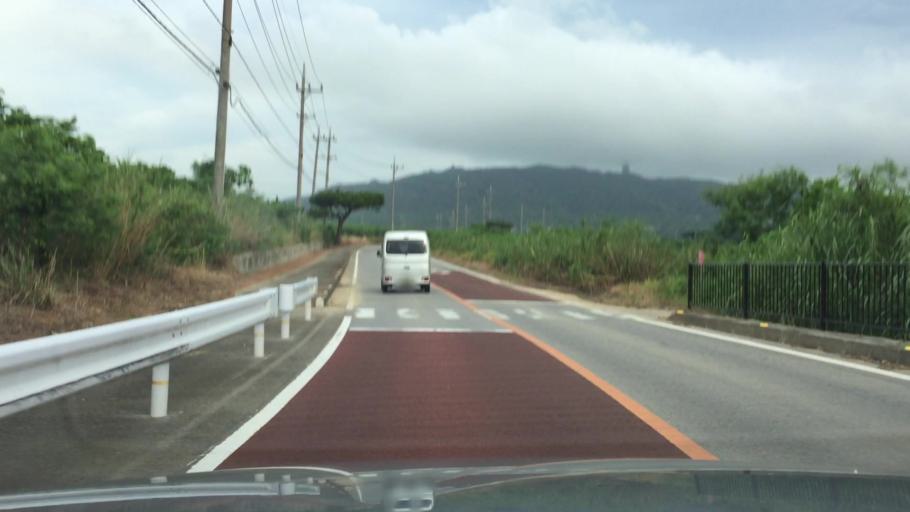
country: JP
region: Okinawa
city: Ishigaki
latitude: 24.4007
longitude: 124.1504
